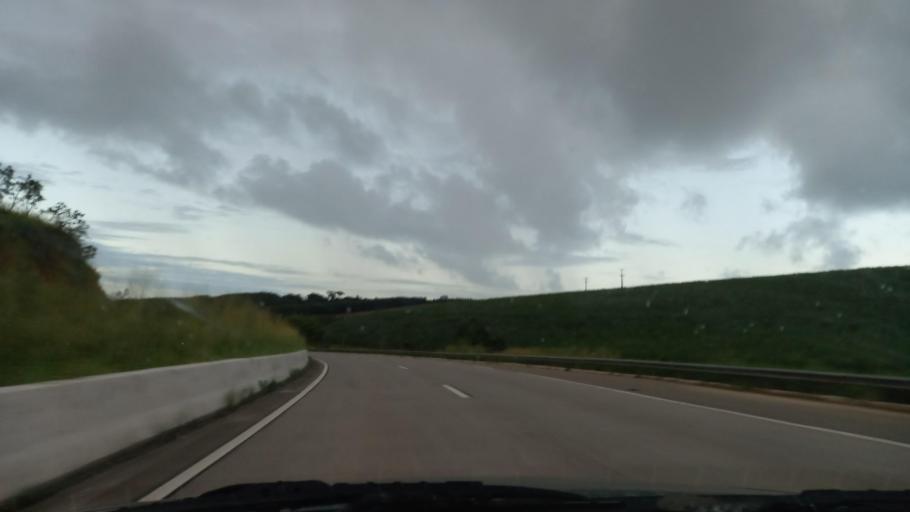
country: BR
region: Pernambuco
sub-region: Joaquim Nabuco
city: Joaquim Nabuco
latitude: -8.5771
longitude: -35.4876
